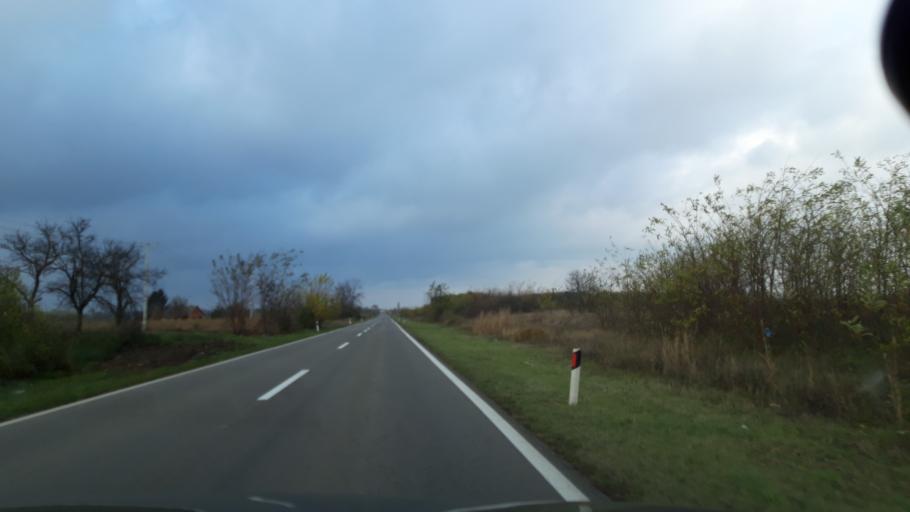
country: RS
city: Sanad
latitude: 45.9703
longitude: 20.1228
